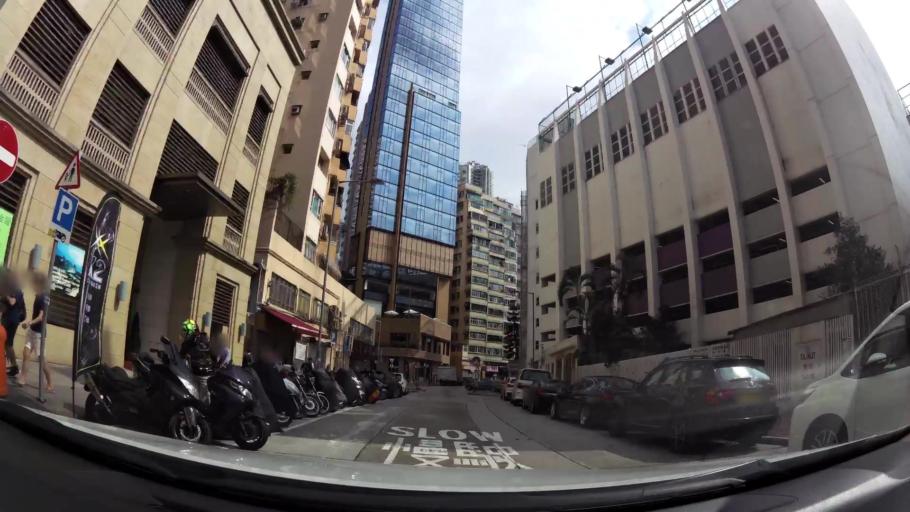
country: HK
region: Wanchai
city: Wan Chai
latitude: 22.2806
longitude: 114.1922
